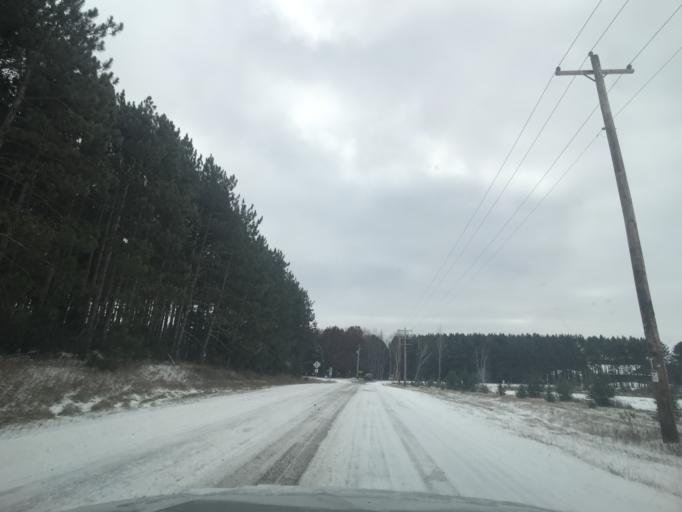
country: US
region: Wisconsin
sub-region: Brown County
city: Suamico
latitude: 44.6928
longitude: -88.1008
